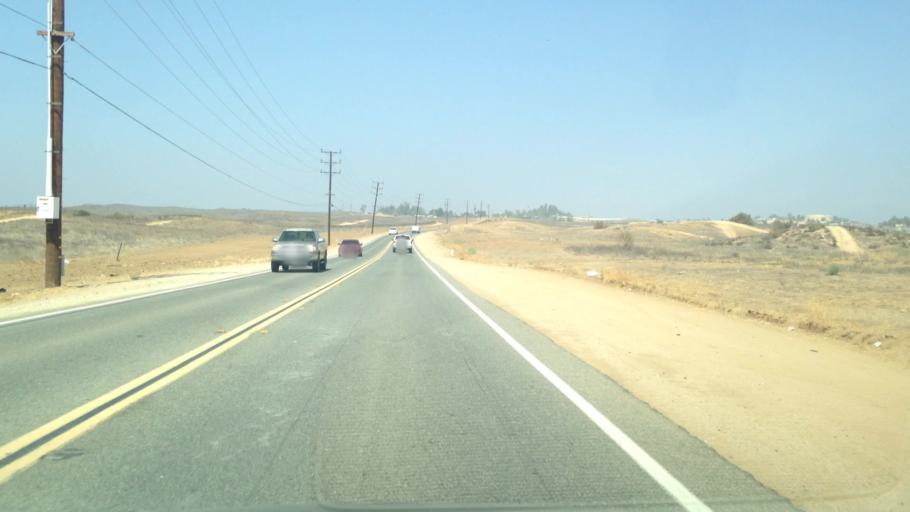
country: US
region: California
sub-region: Riverside County
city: Woodcrest
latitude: 33.8478
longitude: -117.3826
